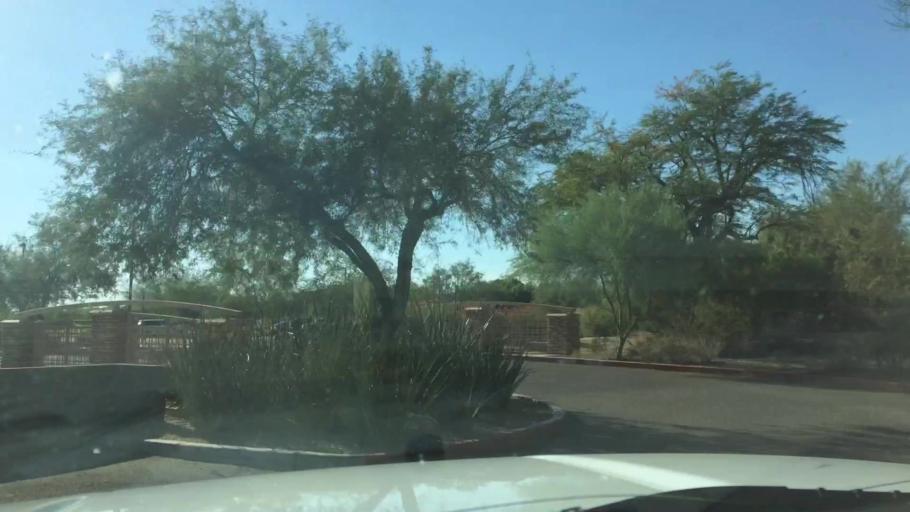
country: US
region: Arizona
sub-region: Maricopa County
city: Paradise Valley
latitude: 33.6450
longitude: -111.9018
